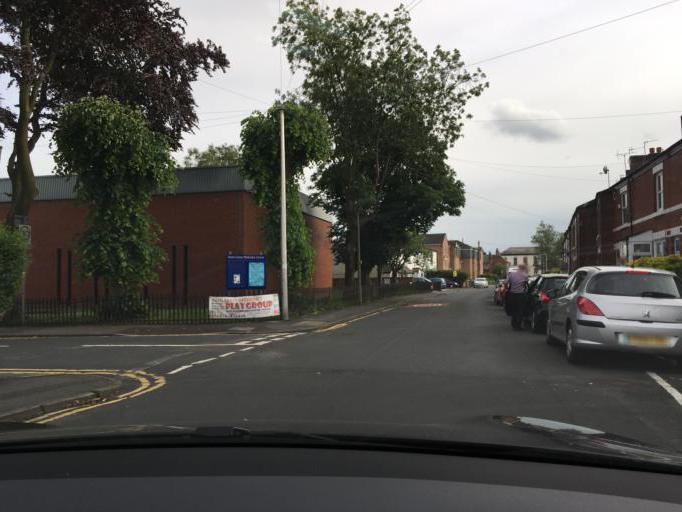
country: GB
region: England
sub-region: Borough of Stockport
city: Hazel Grove
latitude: 53.3813
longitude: -2.1196
